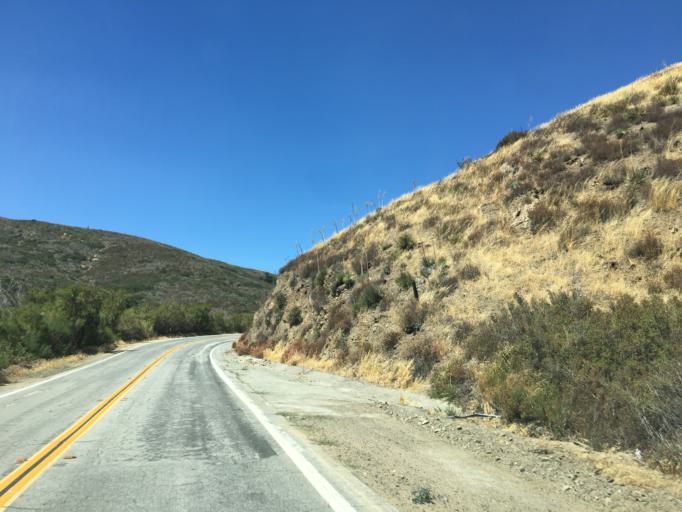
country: US
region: California
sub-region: Los Angeles County
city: Leona Valley
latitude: 34.5881
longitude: -118.2906
